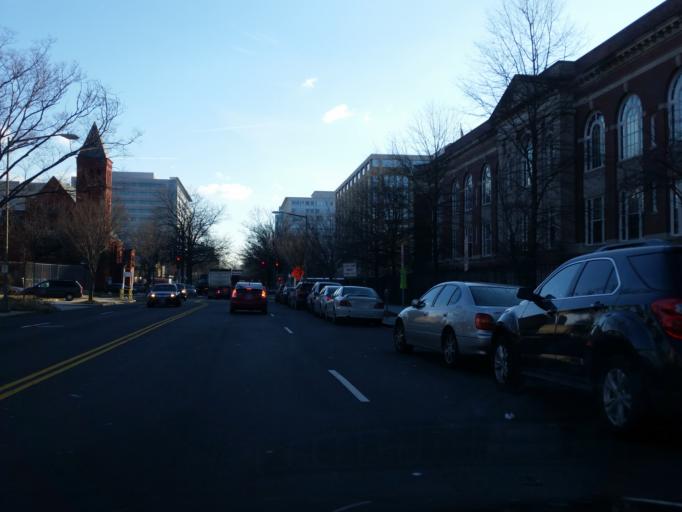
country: US
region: Washington, D.C.
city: Washington, D.C.
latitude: 38.9025
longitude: -77.0104
